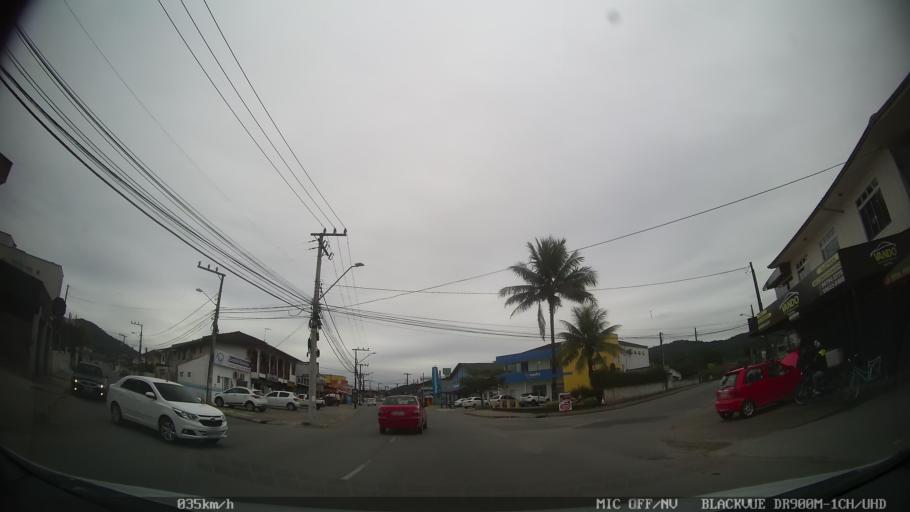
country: BR
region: Santa Catarina
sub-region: Joinville
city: Joinville
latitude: -26.2702
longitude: -48.8137
